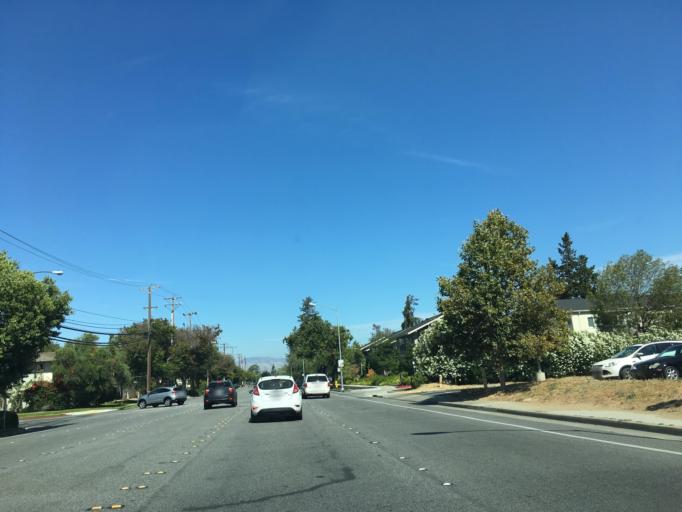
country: US
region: California
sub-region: Santa Clara County
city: Cupertino
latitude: 37.3375
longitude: -122.0405
